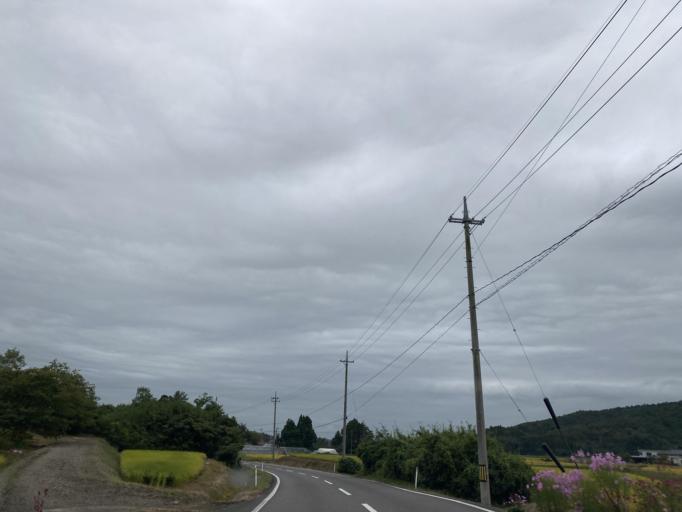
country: JP
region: Fukushima
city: Koriyama
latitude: 37.3593
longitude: 140.2597
